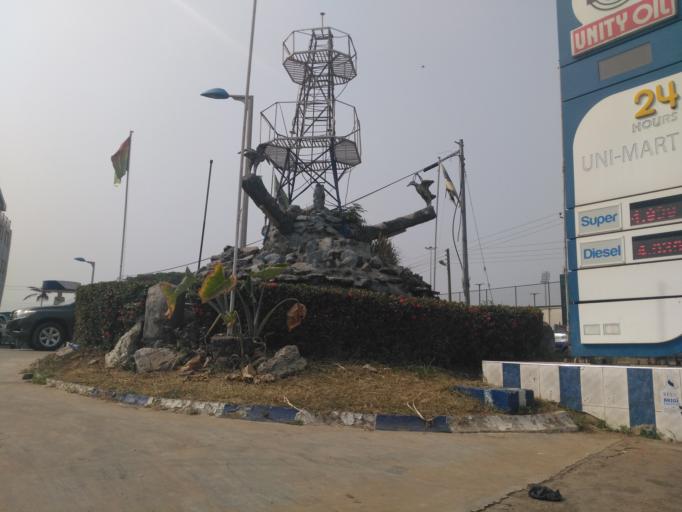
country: GH
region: Ashanti
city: Kumasi
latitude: 6.6803
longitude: -1.6040
